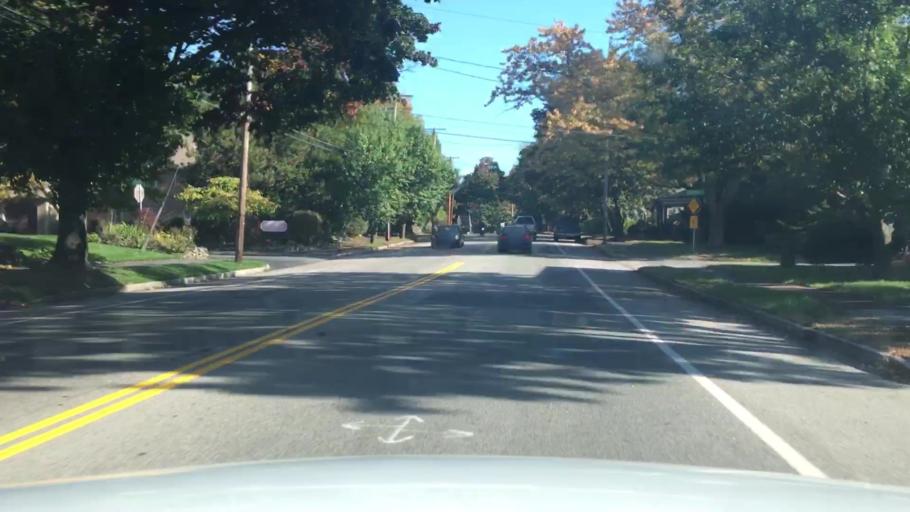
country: US
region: Maine
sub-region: Cumberland County
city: South Portland Gardens
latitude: 43.6645
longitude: -70.2972
